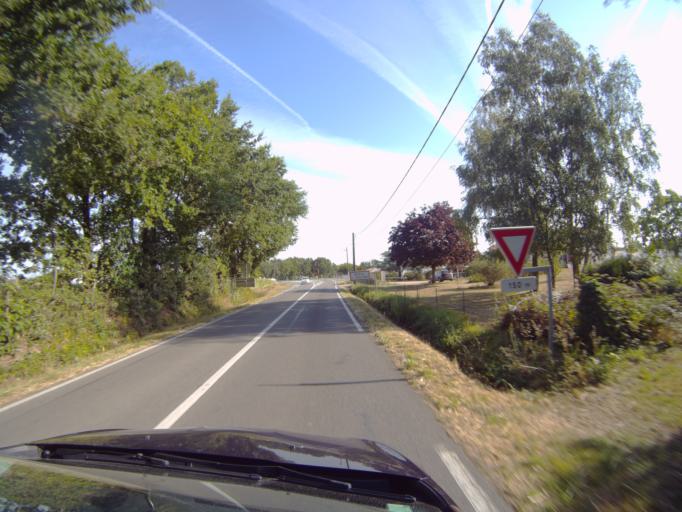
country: FR
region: Pays de la Loire
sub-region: Departement de la Vendee
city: Nieul-le-Dolent
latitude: 46.5691
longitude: -1.5110
